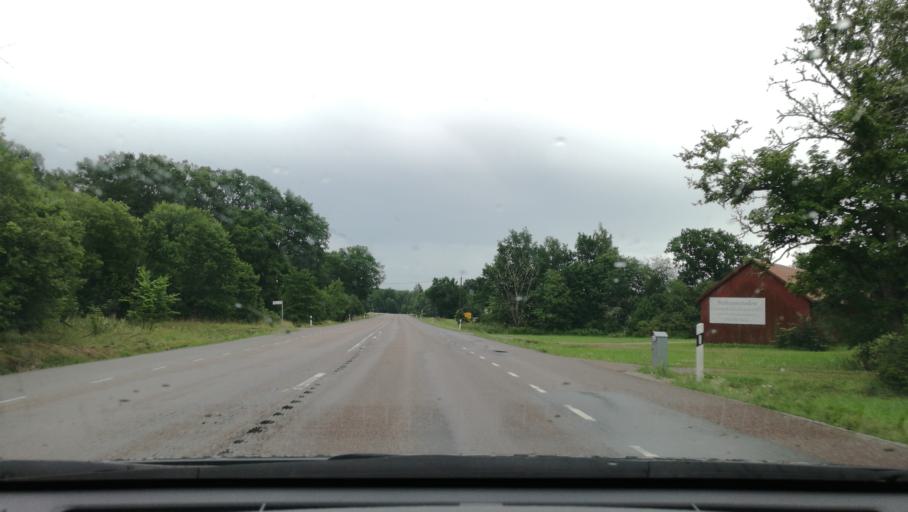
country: SE
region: Vaestmanland
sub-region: Kungsors Kommun
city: Kungsoer
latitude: 59.4423
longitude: 16.0467
